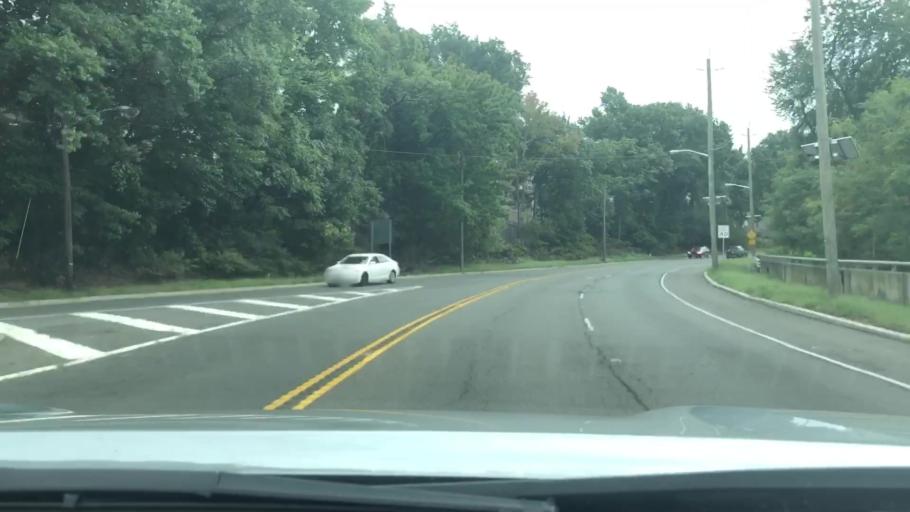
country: US
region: New Jersey
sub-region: Bergen County
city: Palisades Park
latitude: 40.8398
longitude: -73.9922
